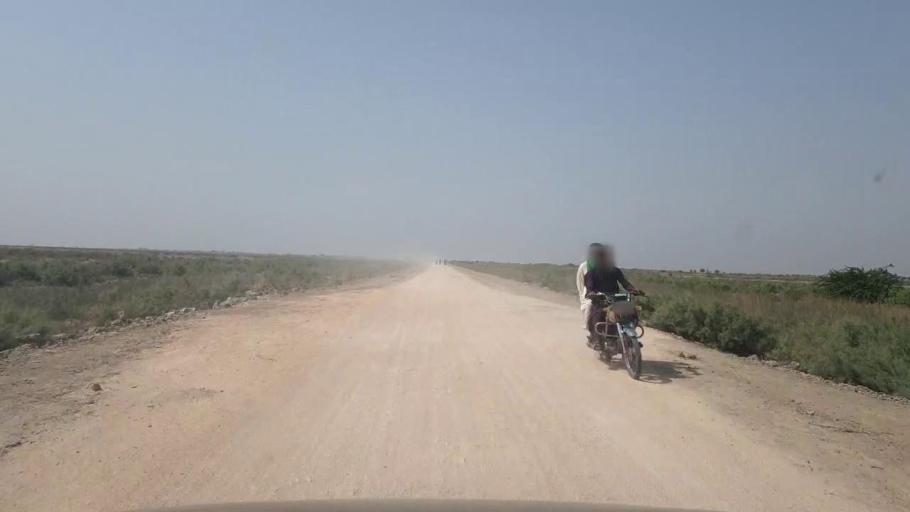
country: PK
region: Sindh
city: Jati
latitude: 24.3766
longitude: 68.5753
